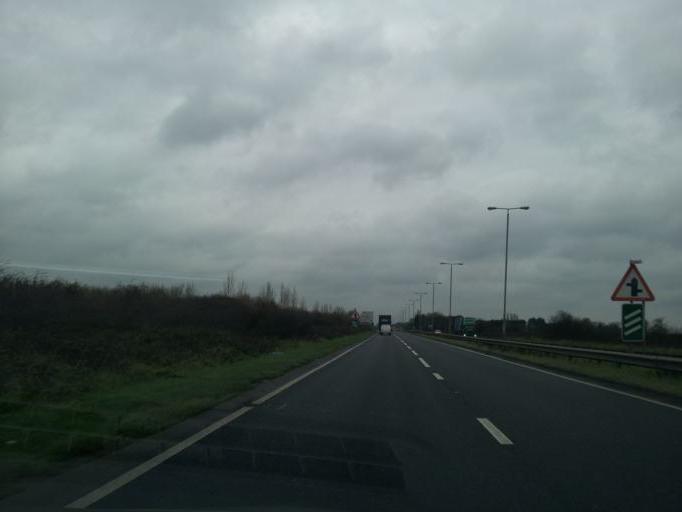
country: GB
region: England
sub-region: Leicestershire
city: Queniborough
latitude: 52.7387
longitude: -1.0669
